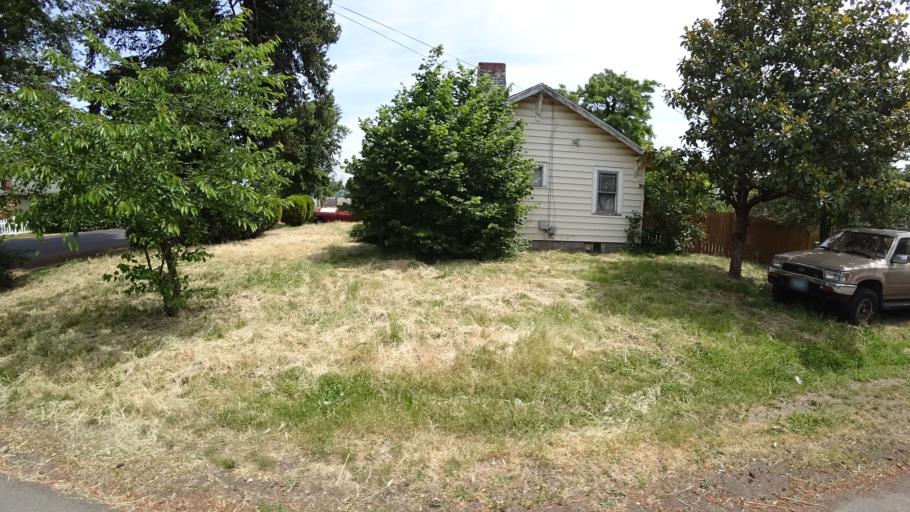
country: US
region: Oregon
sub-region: Multnomah County
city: Lents
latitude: 45.4709
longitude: -122.5933
